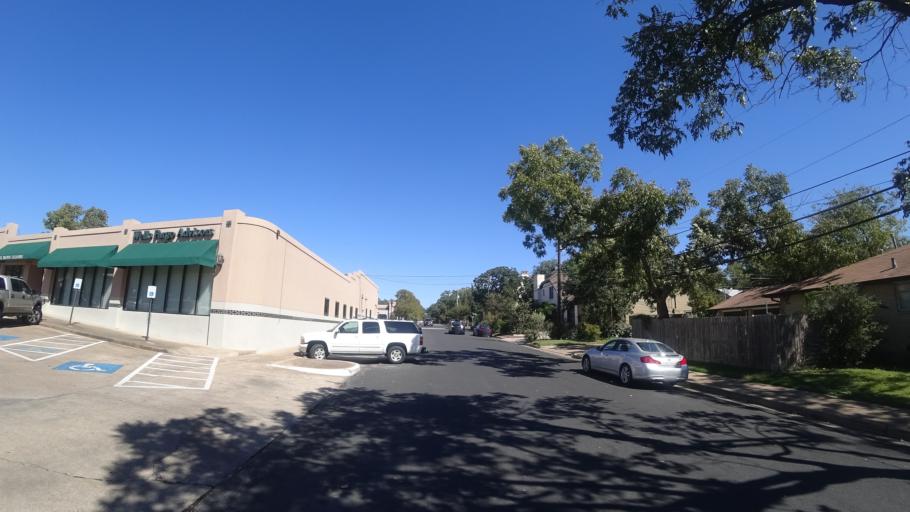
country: US
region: Texas
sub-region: Travis County
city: Rollingwood
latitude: 30.2962
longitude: -97.7675
